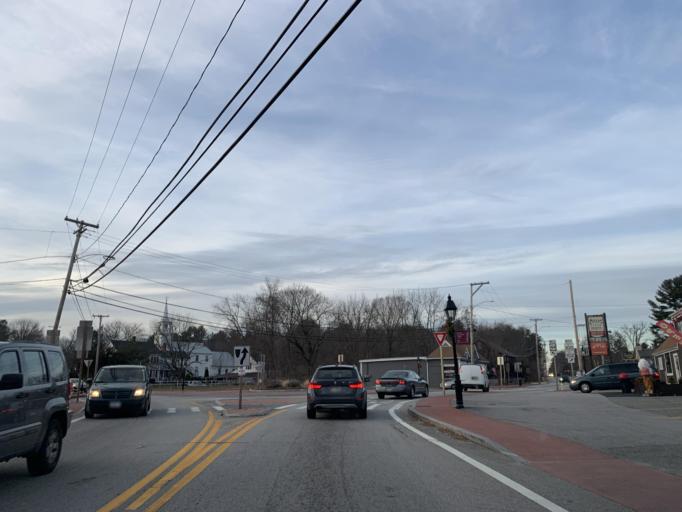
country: US
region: Rhode Island
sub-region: Providence County
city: Chepachet
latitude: 41.9150
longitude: -71.6713
